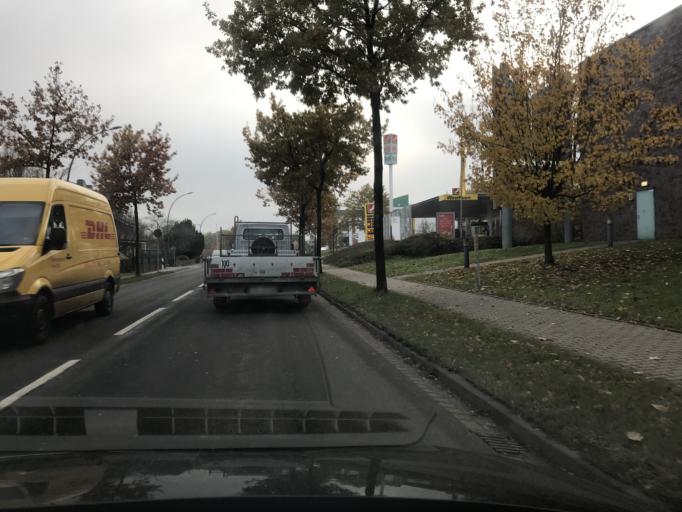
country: DE
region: North Rhine-Westphalia
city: Oelde
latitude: 51.8120
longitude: 8.1348
